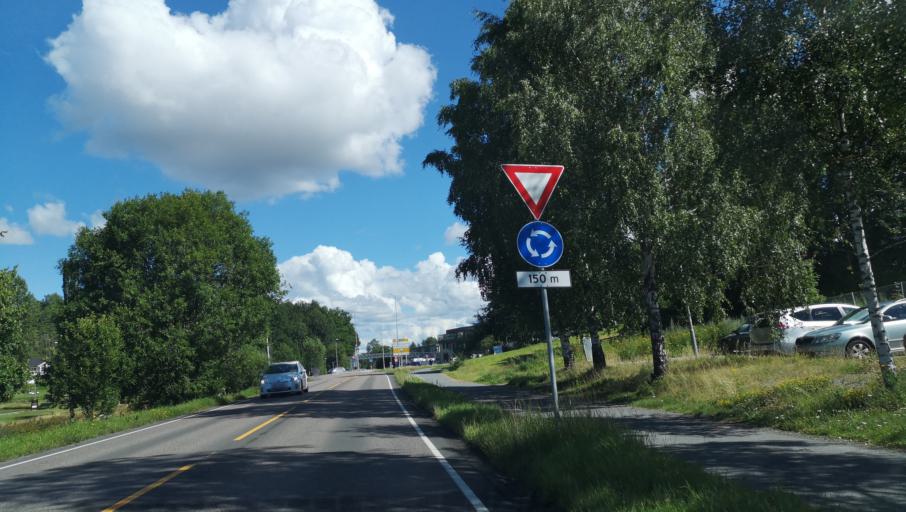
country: NO
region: Akershus
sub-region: Frogn
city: Drobak
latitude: 59.6732
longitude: 10.6525
